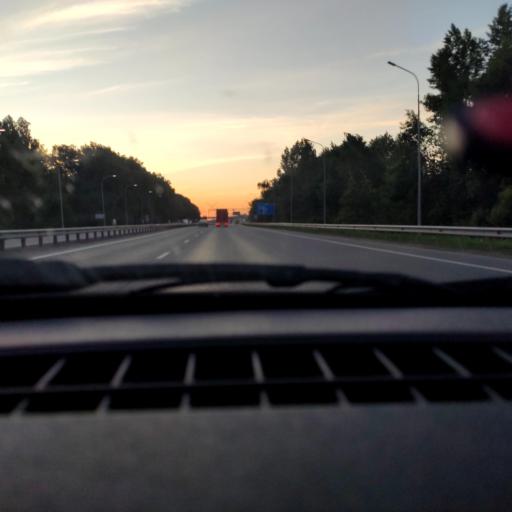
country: RU
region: Bashkortostan
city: Ufa
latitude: 54.5679
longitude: 55.9176
